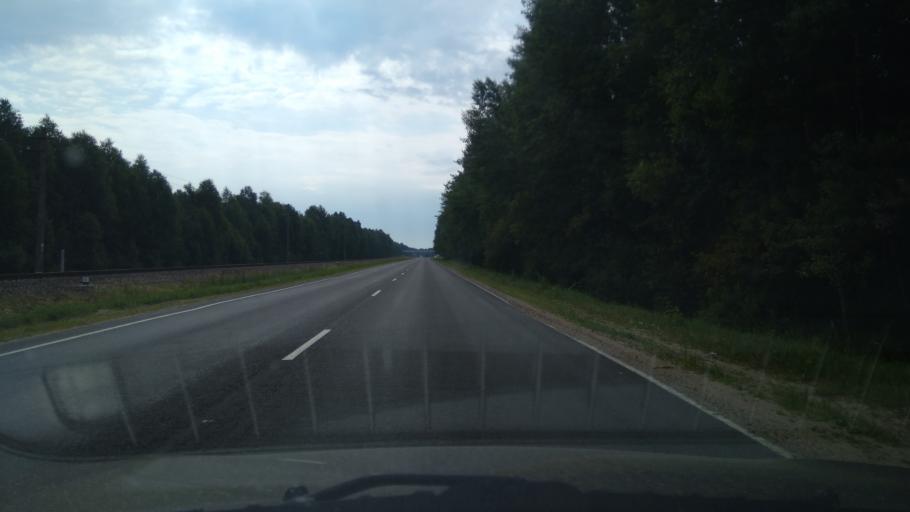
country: BY
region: Brest
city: Nyakhachava
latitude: 52.5826
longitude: 25.1022
